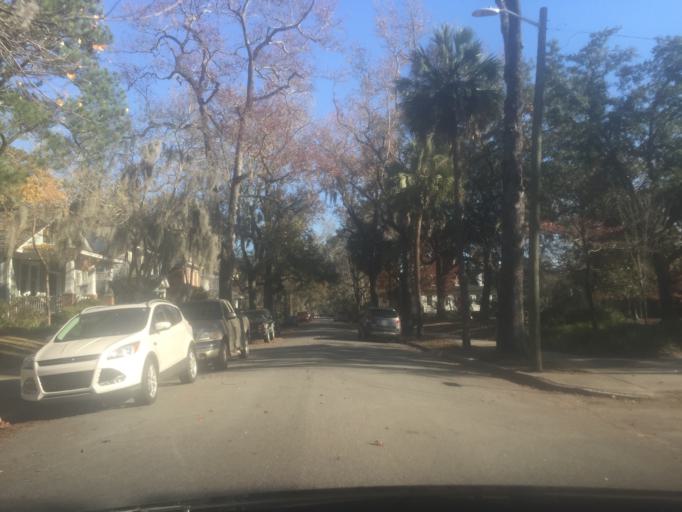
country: US
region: Georgia
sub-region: Chatham County
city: Savannah
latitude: 32.0509
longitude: -81.1018
